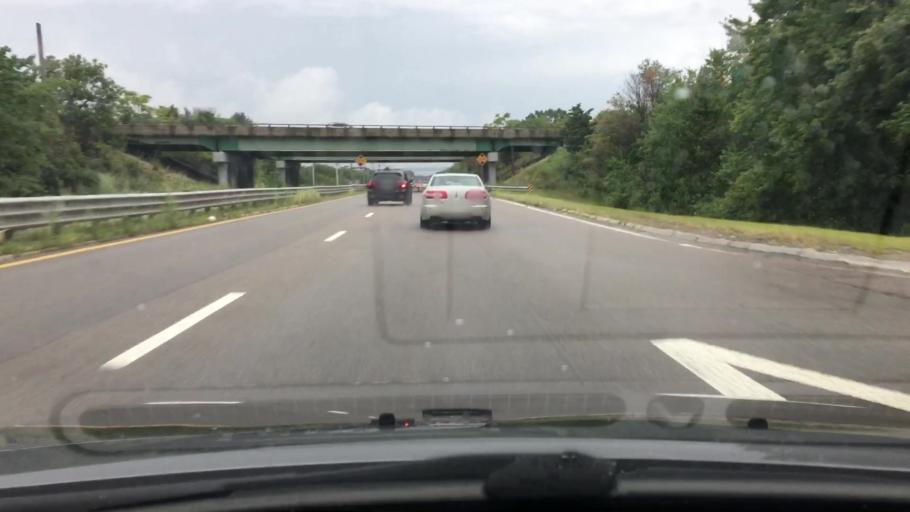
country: US
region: Massachusetts
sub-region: Norfolk County
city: Plainville
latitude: 41.9482
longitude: -71.3461
